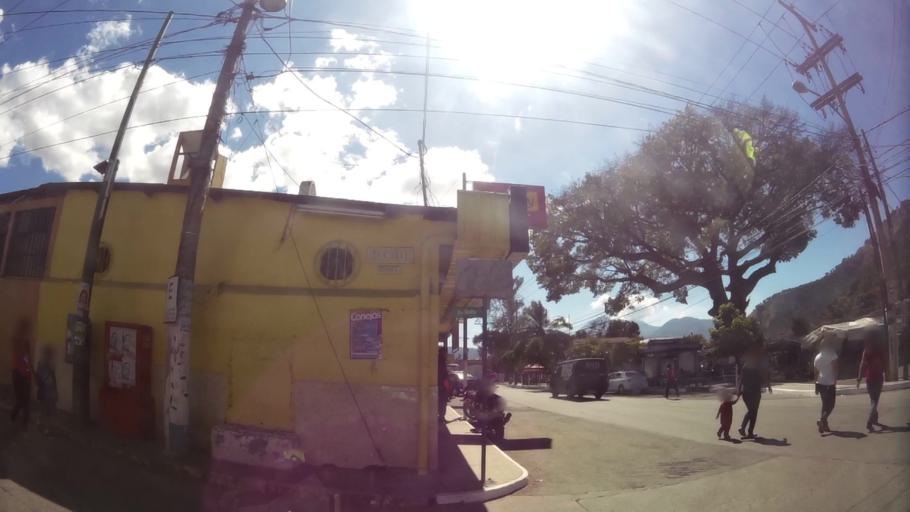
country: GT
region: Guatemala
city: Villa Canales
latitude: 14.4821
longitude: -90.5343
